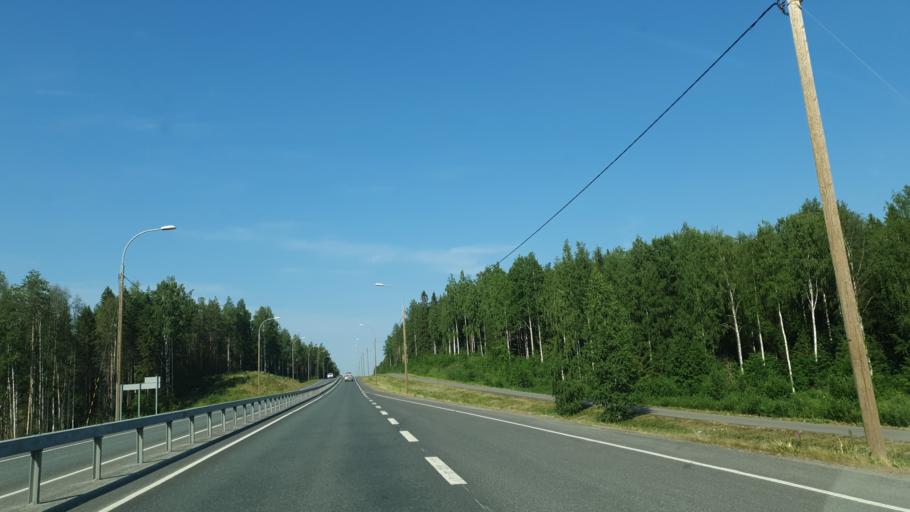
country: FI
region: Northern Savo
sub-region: Kuopio
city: Siilinjaervi
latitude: 63.1009
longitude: 27.7390
